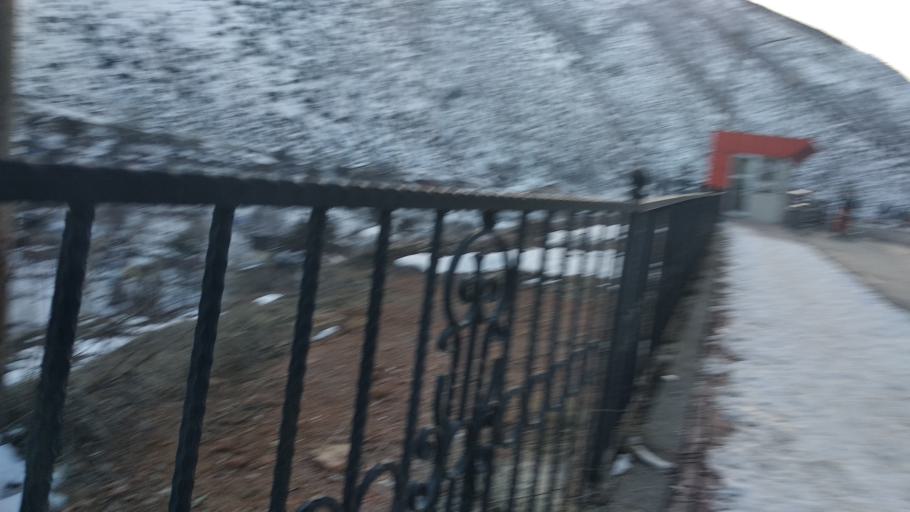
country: TR
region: Gumushane
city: Gumushkhane
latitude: 40.4373
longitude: 39.5122
